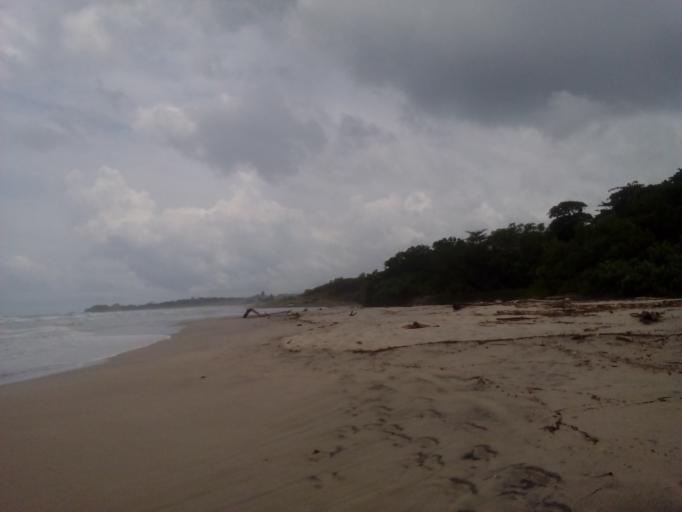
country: CR
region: Guanacaste
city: Samara
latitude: 9.9352
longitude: -85.6654
